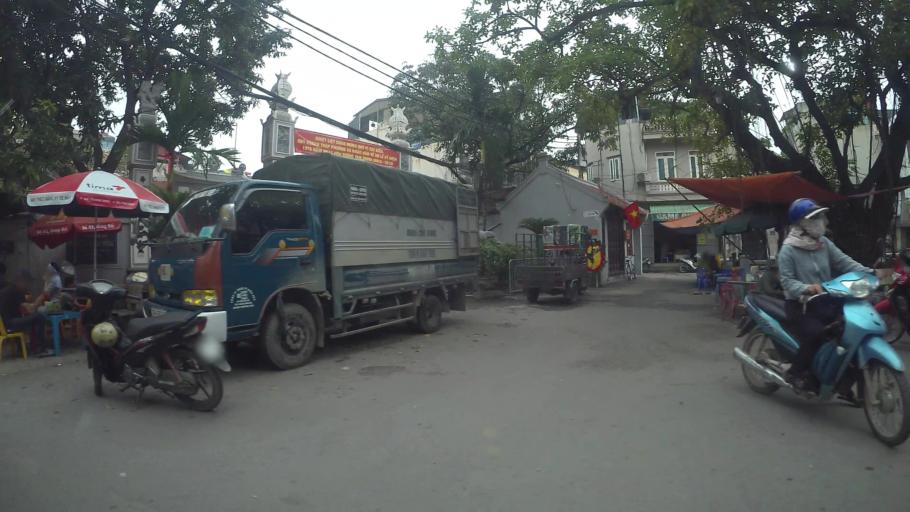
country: VN
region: Ha Noi
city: Hai BaTrung
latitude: 20.9921
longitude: 105.8590
